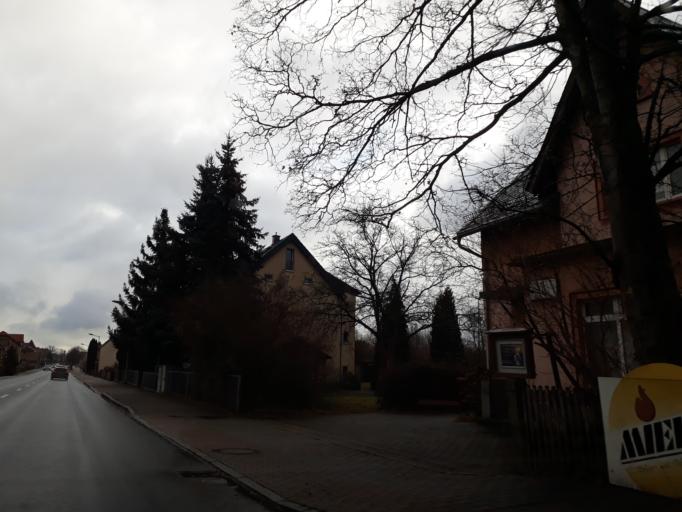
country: DE
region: Saxony
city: Herrnhut
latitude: 51.0231
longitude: 14.7328
